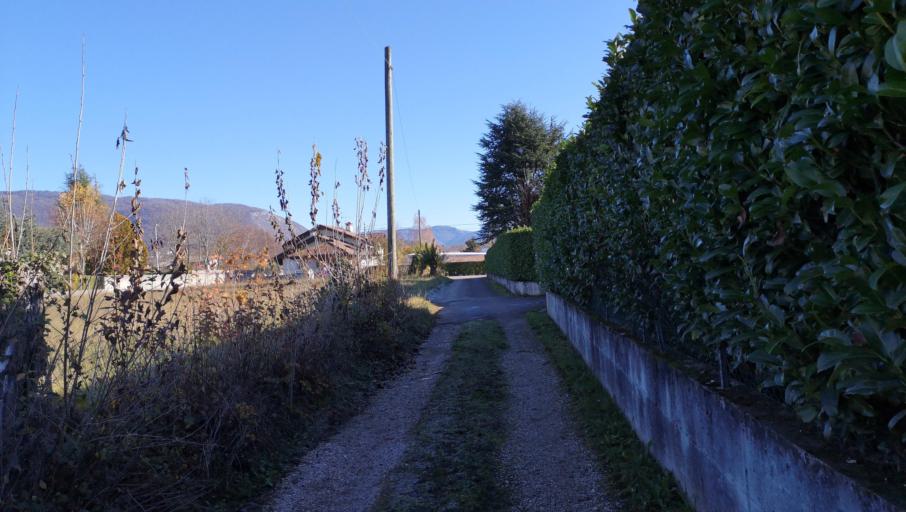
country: IT
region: Friuli Venezia Giulia
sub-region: Provincia di Udine
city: Tarcento
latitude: 46.2107
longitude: 13.2034
